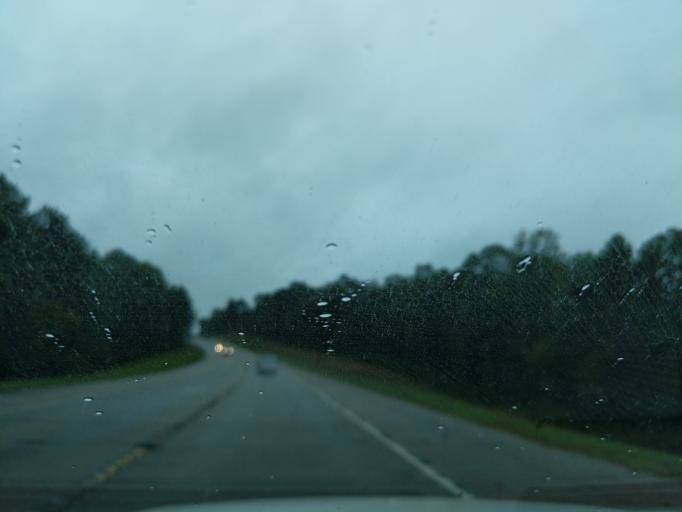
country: US
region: Louisiana
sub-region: Webster Parish
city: Minden
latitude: 32.5978
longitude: -93.2497
